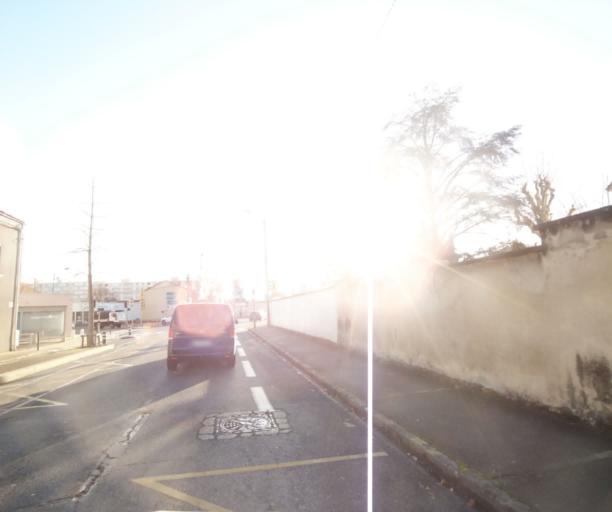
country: FR
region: Rhone-Alpes
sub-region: Departement de la Loire
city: Roanne
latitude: 46.0449
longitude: 4.0792
